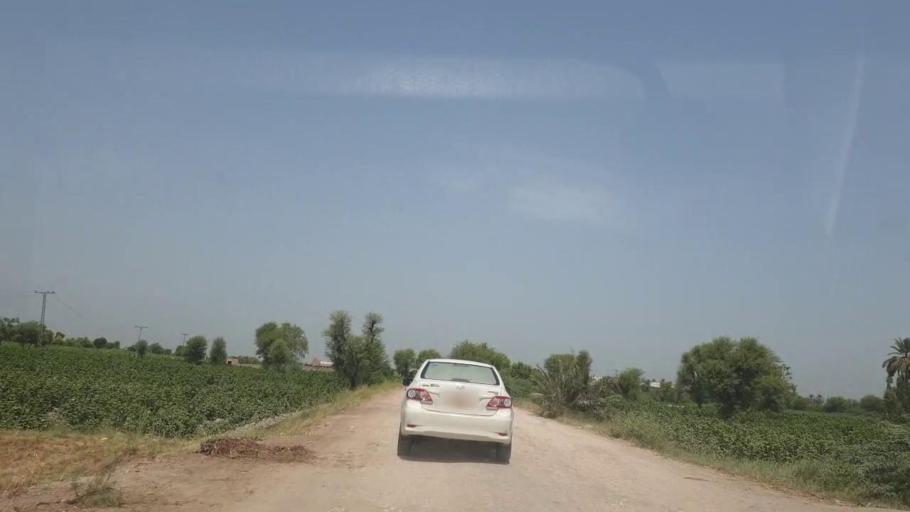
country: PK
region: Sindh
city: Gambat
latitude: 27.2990
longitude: 68.6086
